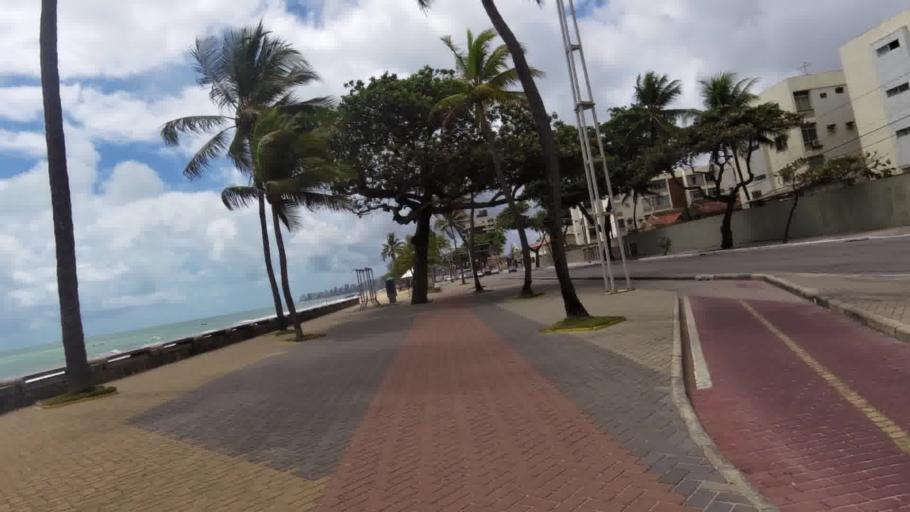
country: BR
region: Pernambuco
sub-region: Recife
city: Recife
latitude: -8.1477
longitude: -34.9063
